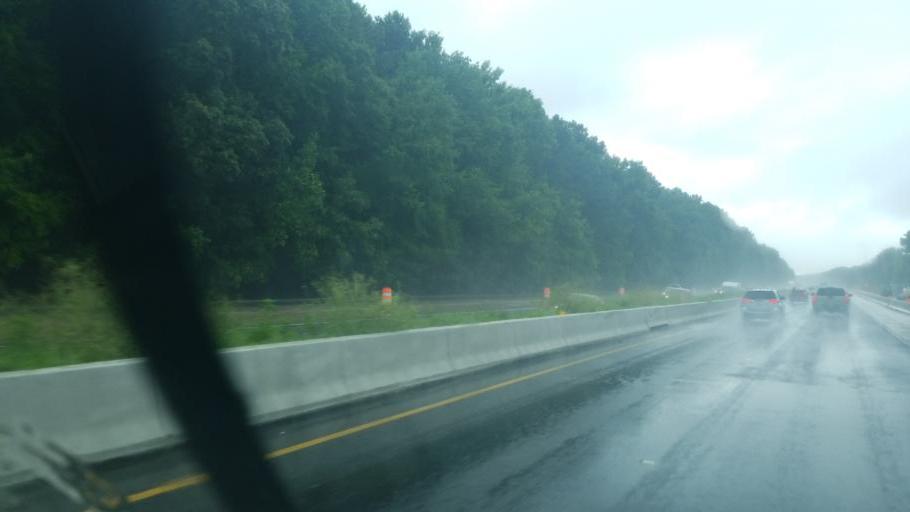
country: US
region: Virginia
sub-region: York County
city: Yorktown
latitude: 37.1474
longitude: -76.5337
